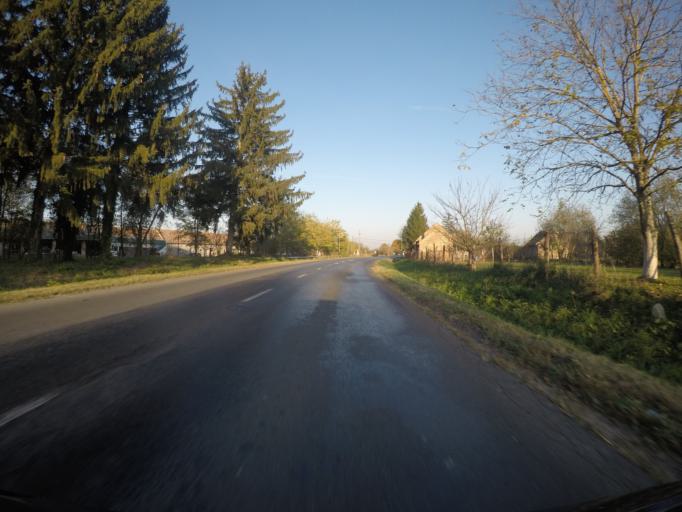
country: HU
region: Somogy
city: Barcs
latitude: 46.0170
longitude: 17.6216
